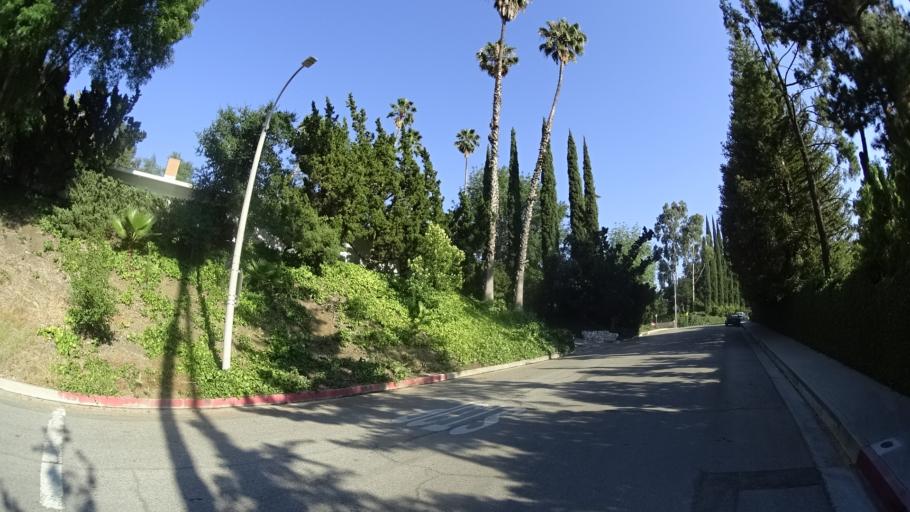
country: US
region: California
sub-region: Los Angeles County
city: Universal City
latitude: 34.1296
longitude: -118.3862
